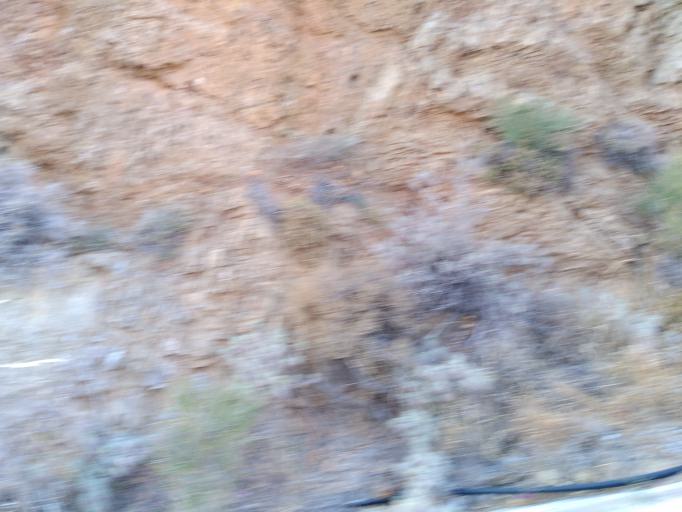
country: GR
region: South Aegean
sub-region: Nomos Kykladon
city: Amorgos
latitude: 36.9100
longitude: 25.9768
